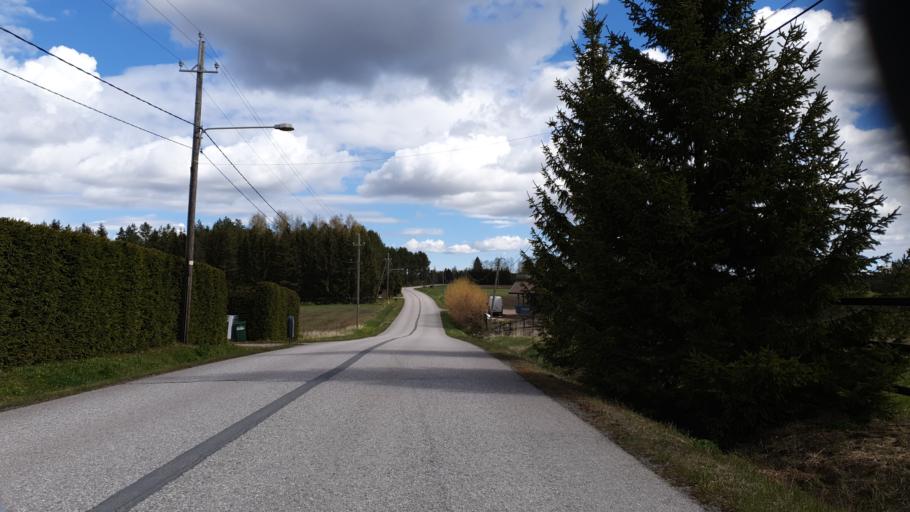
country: FI
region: Uusimaa
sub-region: Helsinki
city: Tuusula
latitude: 60.3938
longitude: 24.9159
